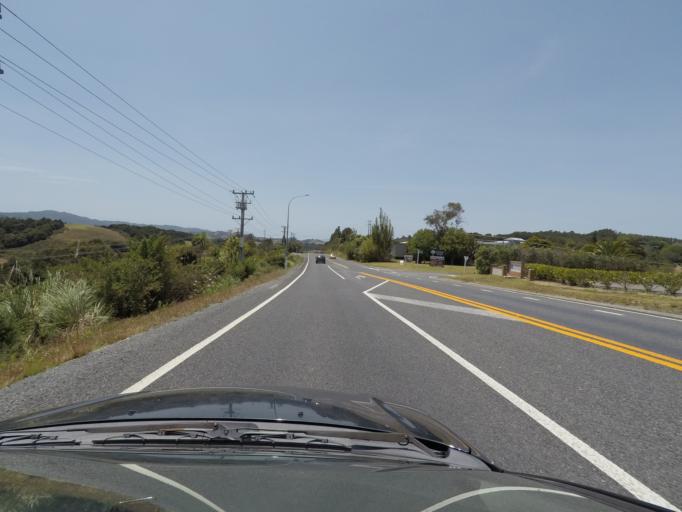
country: NZ
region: Auckland
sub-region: Auckland
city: Warkworth
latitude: -36.3767
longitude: 174.6713
